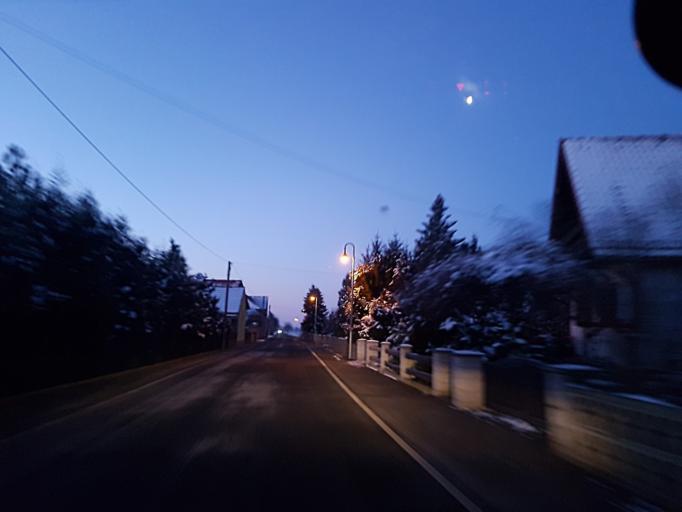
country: DE
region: Brandenburg
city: Falkenberg
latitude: 51.5171
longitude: 13.2980
